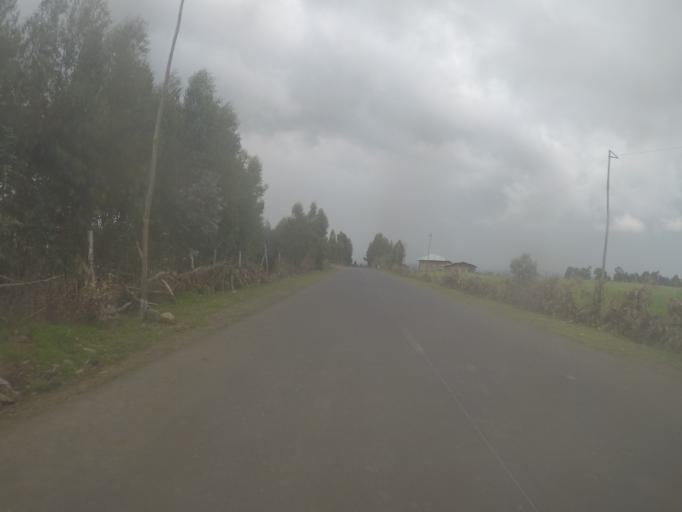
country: ET
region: Amhara
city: Dabat
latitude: 12.9429
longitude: 37.7453
